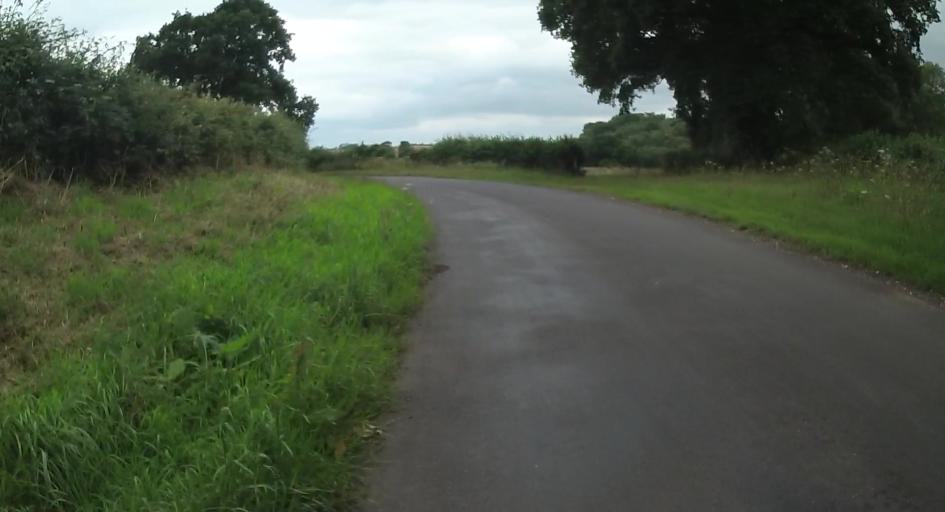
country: GB
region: England
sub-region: Hampshire
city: Swanmore
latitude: 51.0262
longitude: -1.1682
